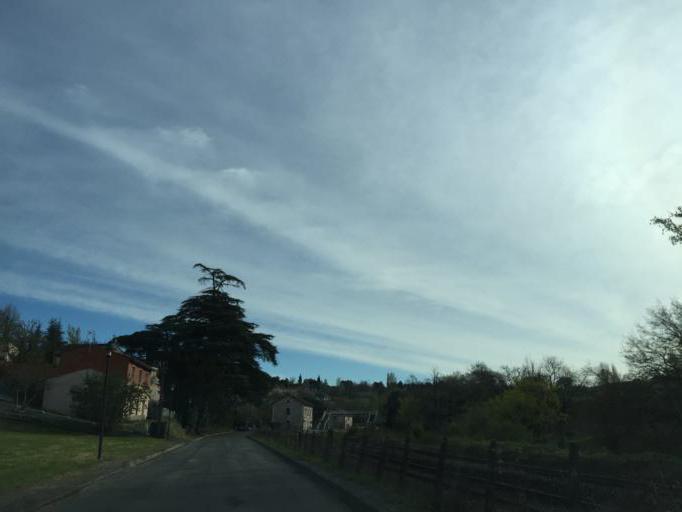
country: FR
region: Midi-Pyrenees
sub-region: Departement de la Haute-Garonne
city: Montastruc-la-Conseillere
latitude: 43.7148
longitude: 1.5963
